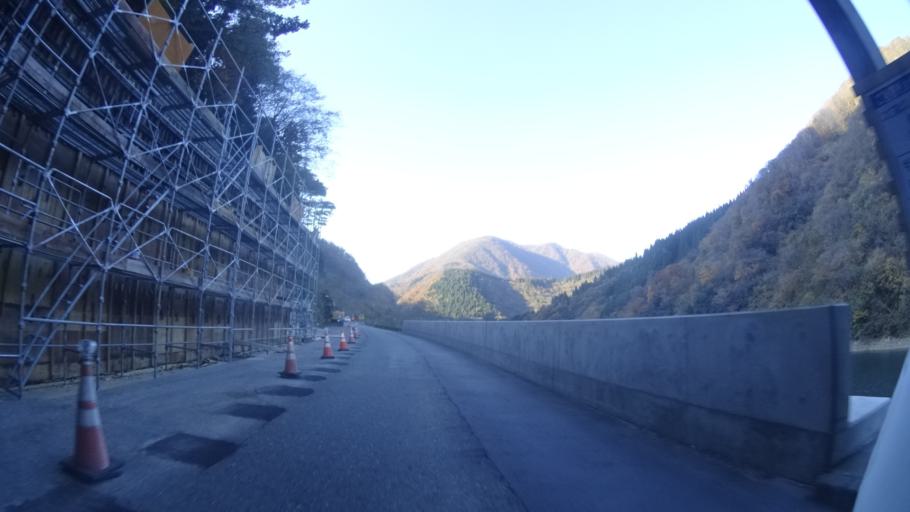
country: JP
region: Fukui
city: Ono
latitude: 35.9488
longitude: 136.6252
